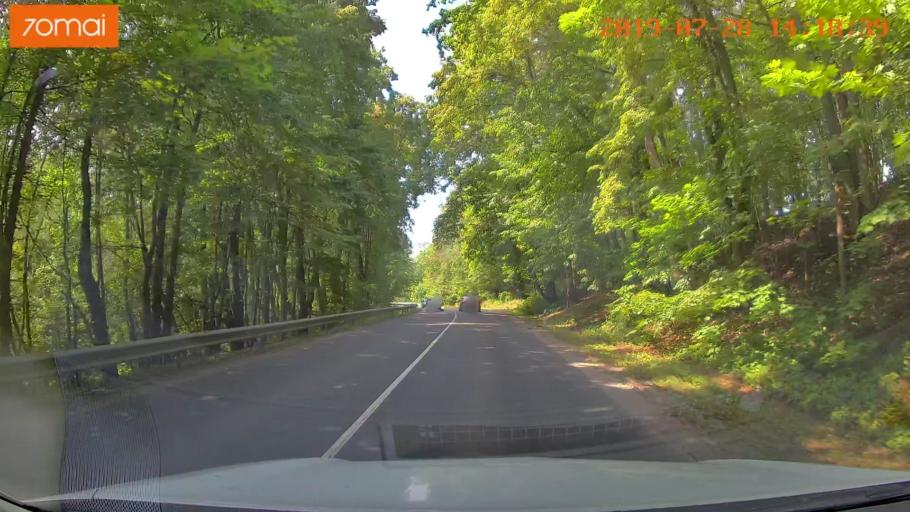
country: RU
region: Kaliningrad
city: Volochayevskoye
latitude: 54.8180
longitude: 20.2371
